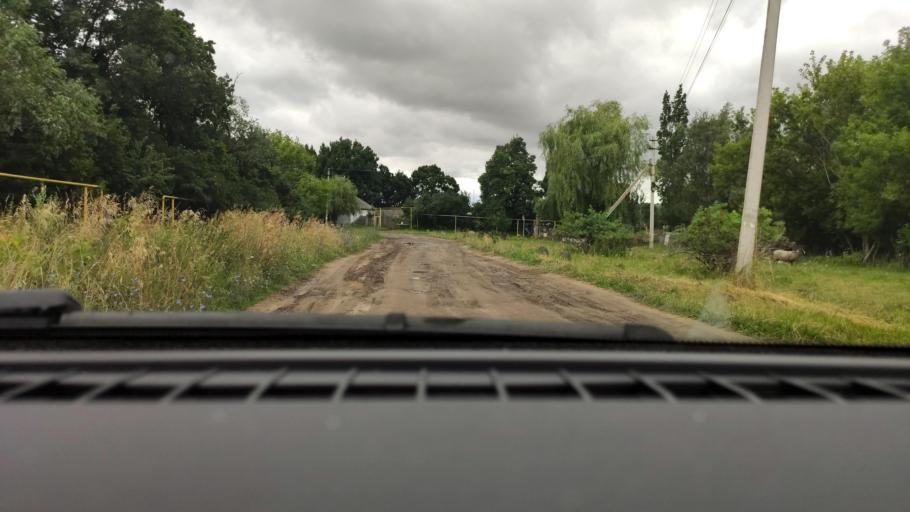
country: RU
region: Voronezj
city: Zemlyansk
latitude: 51.9116
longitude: 38.7254
